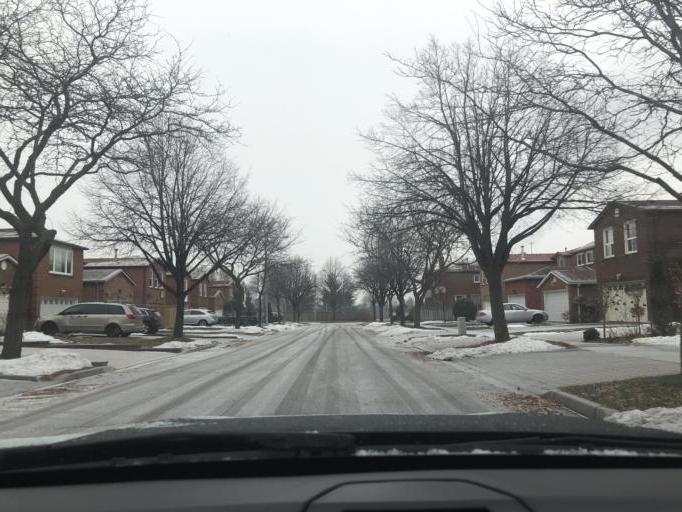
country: CA
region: Ontario
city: Scarborough
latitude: 43.7819
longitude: -79.2671
